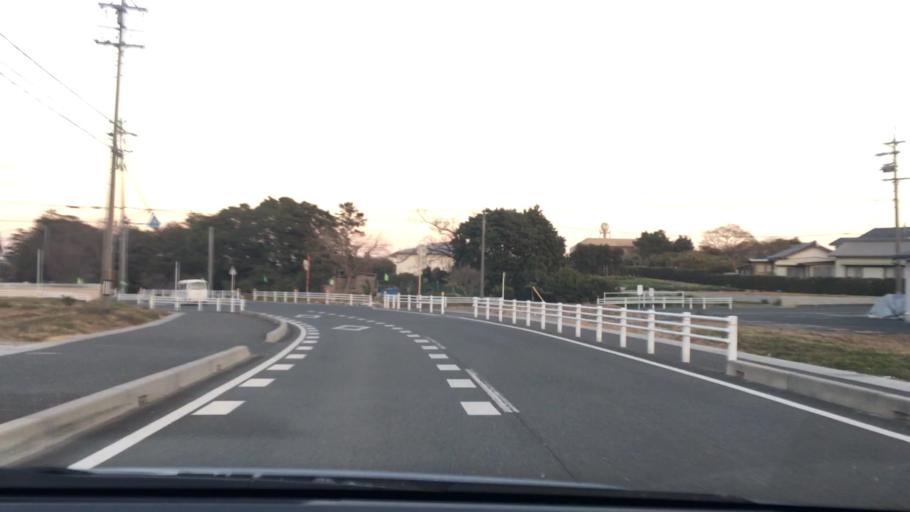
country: JP
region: Aichi
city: Tahara
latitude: 34.6696
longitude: 137.2535
